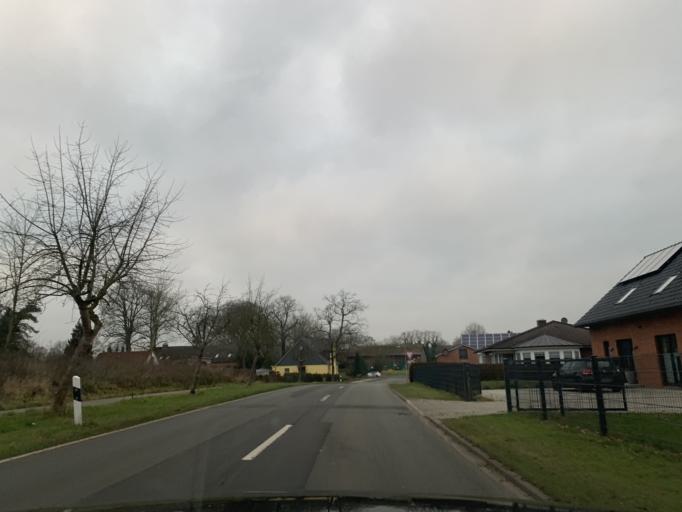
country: DE
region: Schleswig-Holstein
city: Gronwohld
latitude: 53.6665
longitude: 10.4040
